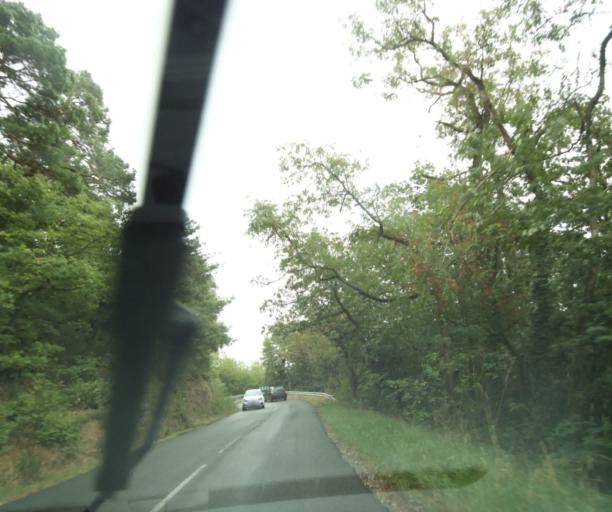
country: FR
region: Auvergne
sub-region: Departement du Puy-de-Dome
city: Durtol
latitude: 45.7937
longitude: 3.0397
